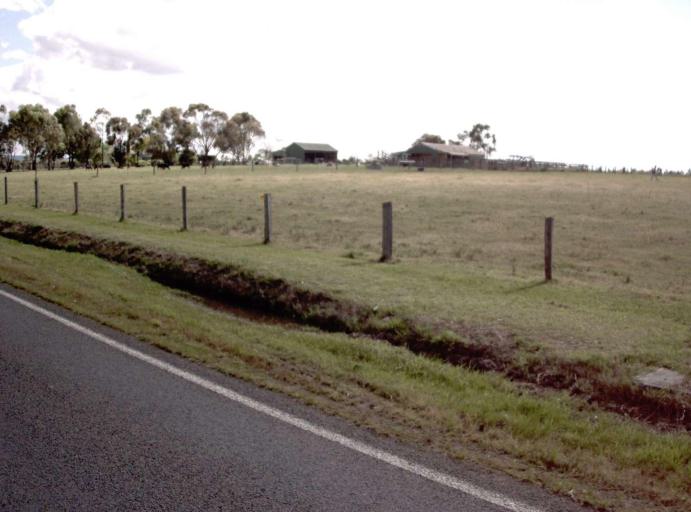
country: AU
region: Victoria
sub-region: Latrobe
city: Morwell
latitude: -38.2852
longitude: 146.4307
